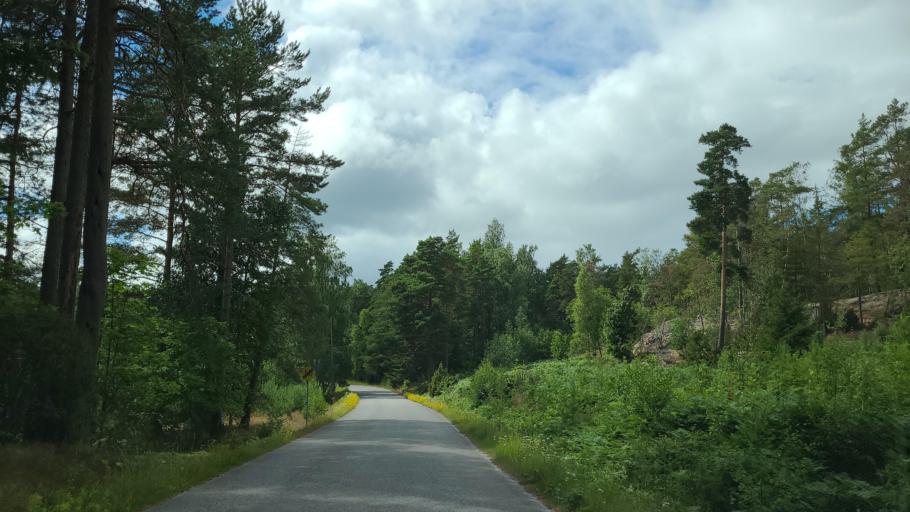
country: FI
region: Varsinais-Suomi
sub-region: Aboland-Turunmaa
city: Nagu
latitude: 60.1650
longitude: 22.0343
